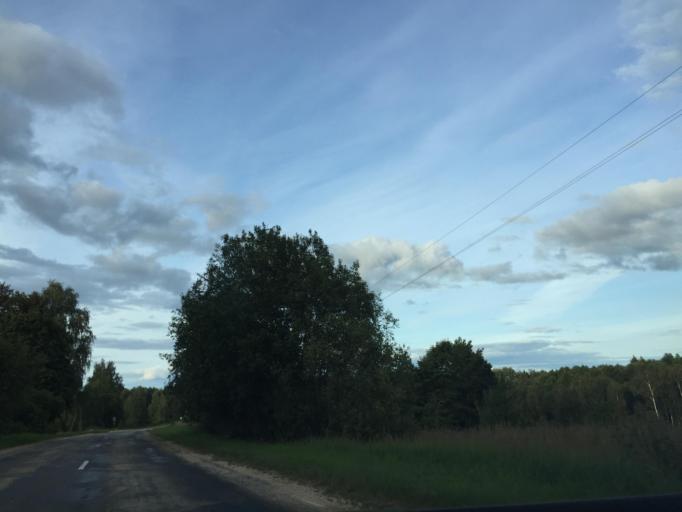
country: LV
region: Nereta
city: Nereta
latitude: 56.2485
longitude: 25.3335
